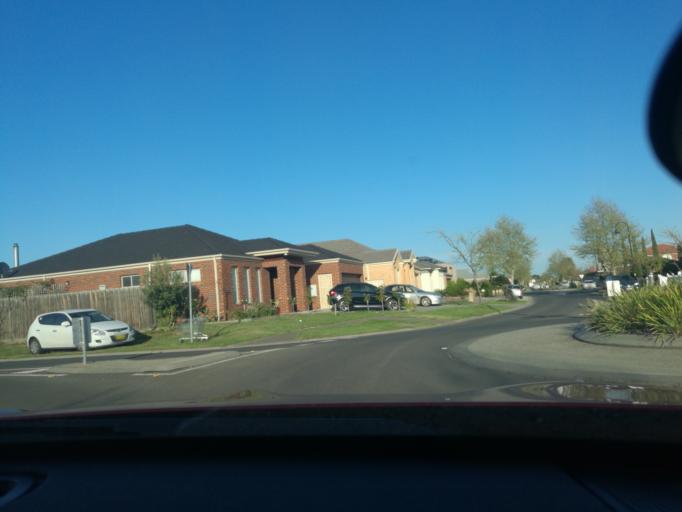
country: AU
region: Victoria
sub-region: Wyndham
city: Williams Landing
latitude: -37.8775
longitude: 144.7459
